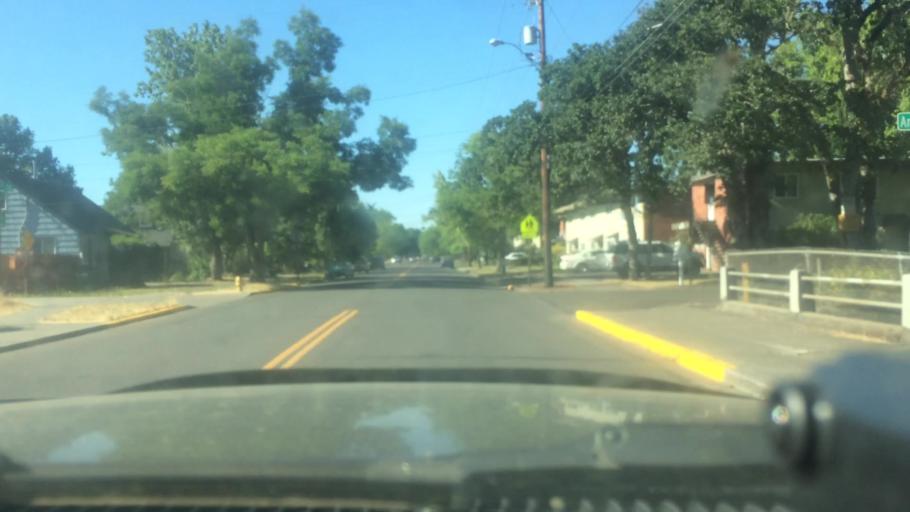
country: US
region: Oregon
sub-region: Lane County
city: Eugene
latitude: 44.0420
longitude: -123.1125
